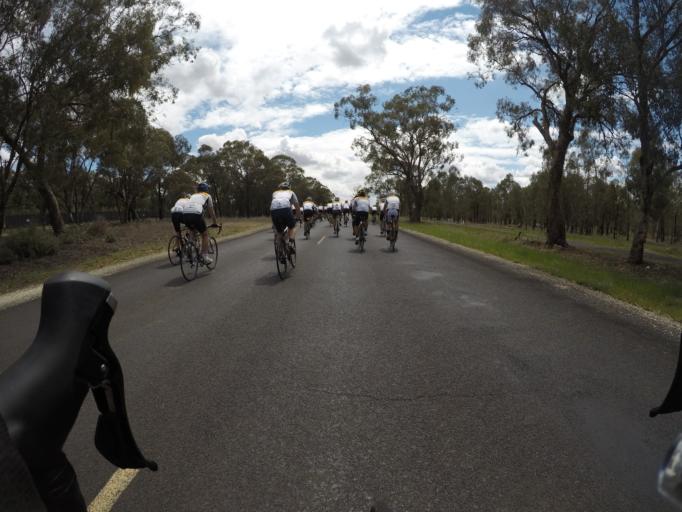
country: AU
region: New South Wales
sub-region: Dubbo Municipality
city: Dubbo
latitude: -32.2787
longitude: 148.5923
